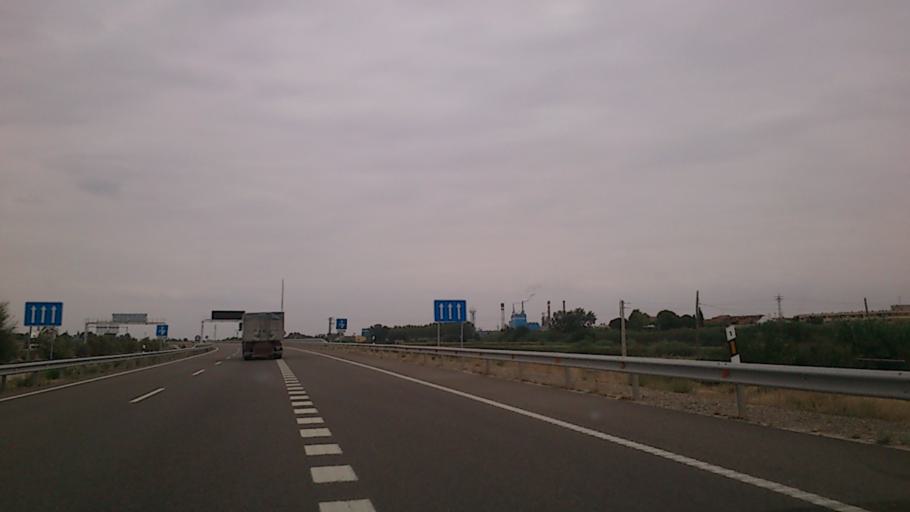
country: ES
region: Aragon
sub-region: Provincia de Zaragoza
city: Zaragoza
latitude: 41.6827
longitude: -0.8334
